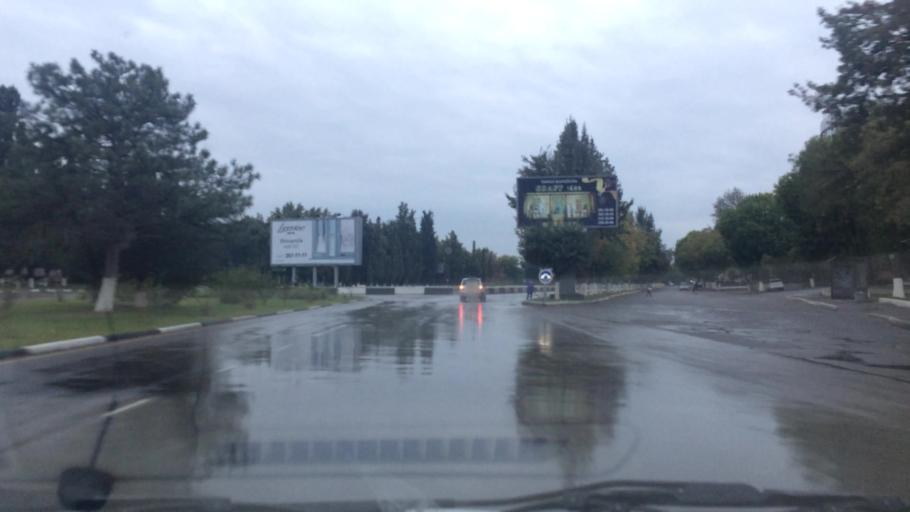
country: UZ
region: Toshkent Shahri
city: Tashkent
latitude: 41.3110
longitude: 69.2402
